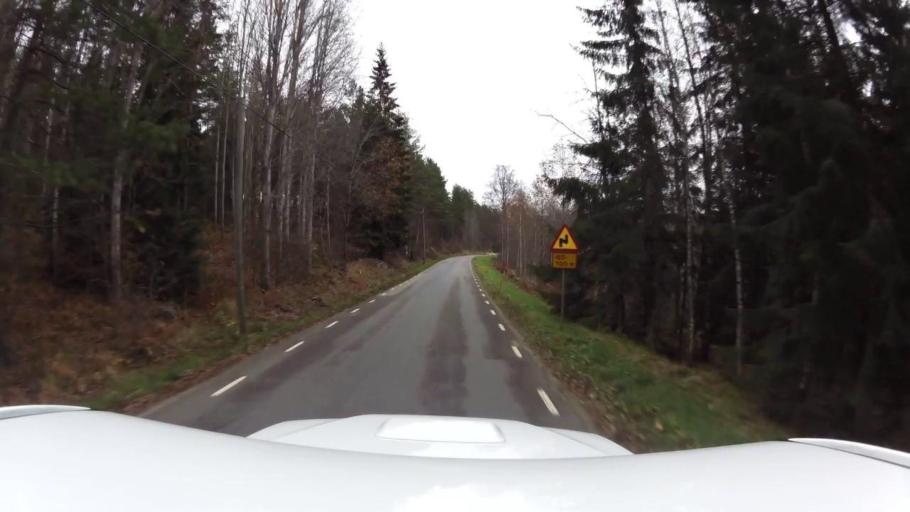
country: SE
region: OEstergoetland
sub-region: Kinda Kommun
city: Rimforsa
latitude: 58.1390
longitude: 15.6290
